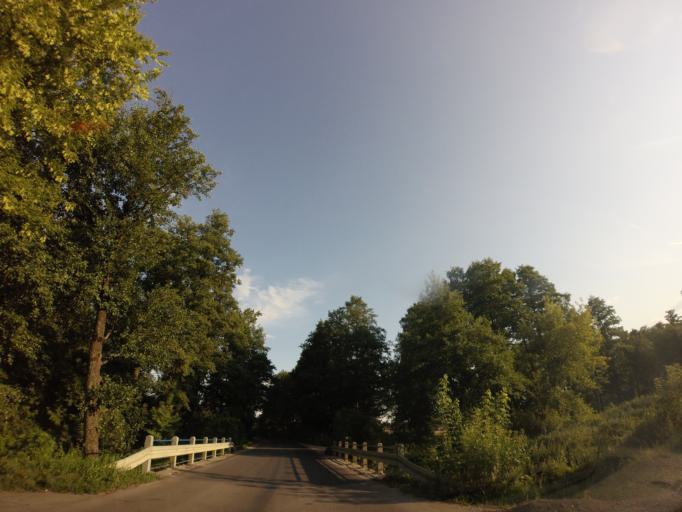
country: PL
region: Lublin Voivodeship
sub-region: Powiat pulawski
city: Kurow
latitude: 51.4183
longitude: 22.2269
